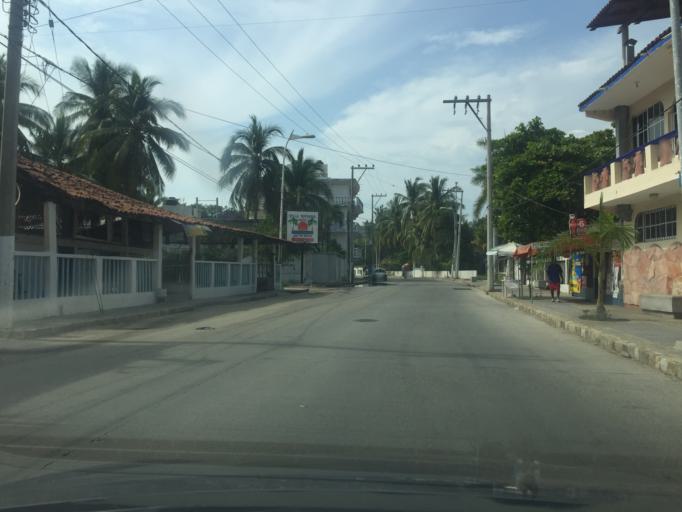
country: MX
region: Guerrero
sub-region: Coyuca de Benitez
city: Colonia Luces en el Mar
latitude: 16.8992
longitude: -99.9662
